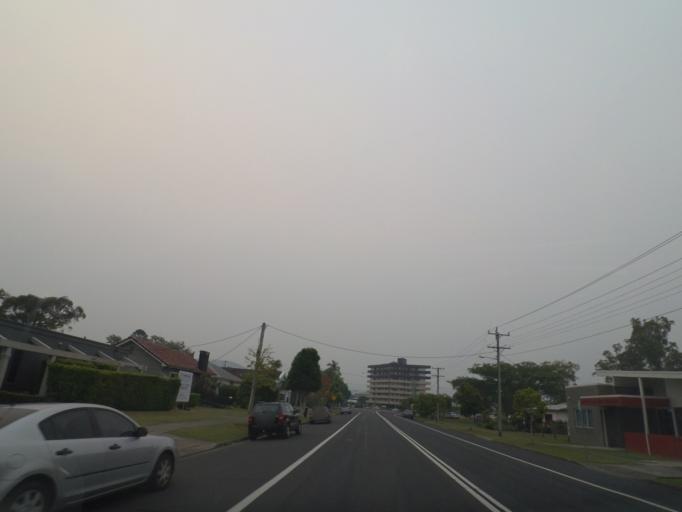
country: AU
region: New South Wales
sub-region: Coffs Harbour
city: Coffs Harbour
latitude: -30.3006
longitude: 153.1157
